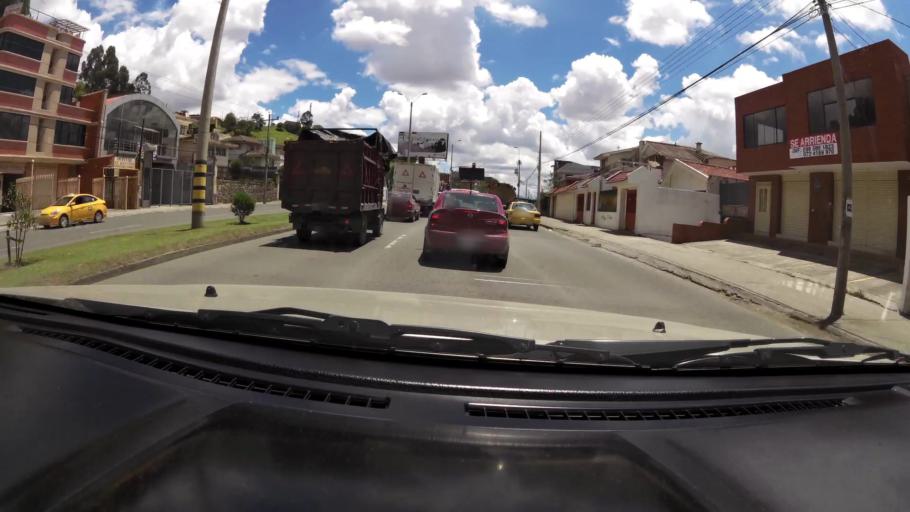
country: EC
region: Azuay
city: Cuenca
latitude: -2.8887
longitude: -79.0171
